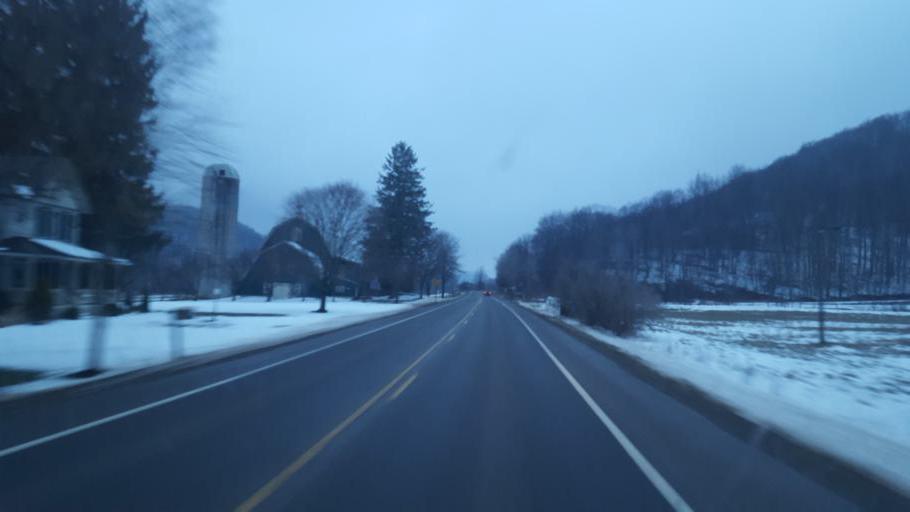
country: US
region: Pennsylvania
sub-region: Potter County
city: Coudersport
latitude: 41.7434
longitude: -78.0852
